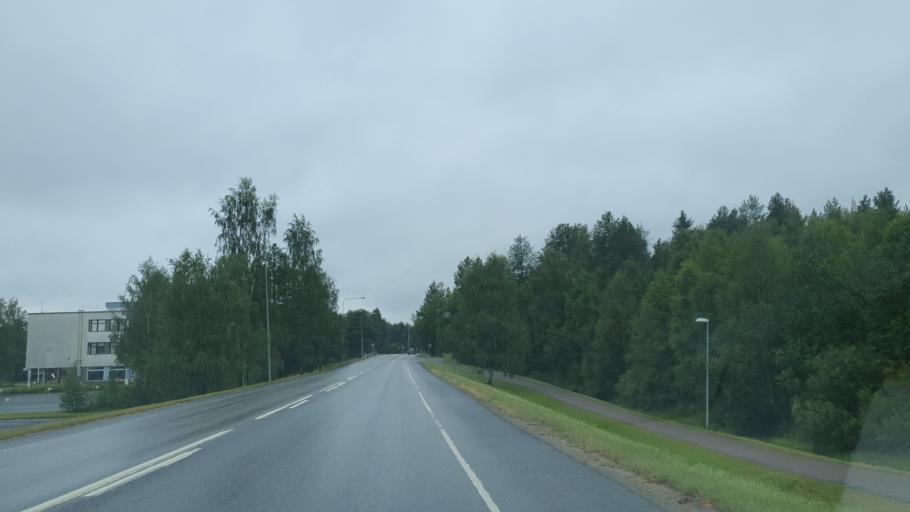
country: FI
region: Lapland
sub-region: Itae-Lappi
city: Kemijaervi
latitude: 66.7197
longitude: 27.3920
